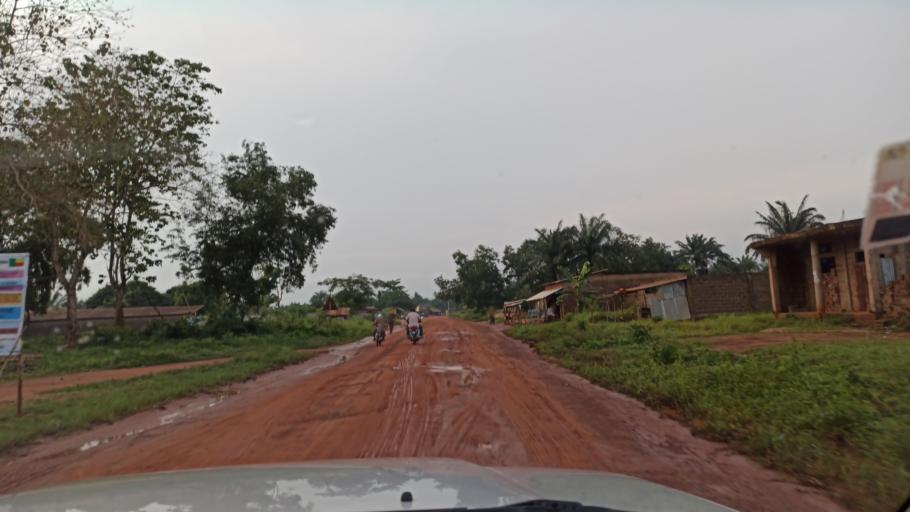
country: BJ
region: Queme
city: Porto-Novo
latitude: 6.5455
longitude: 2.6163
